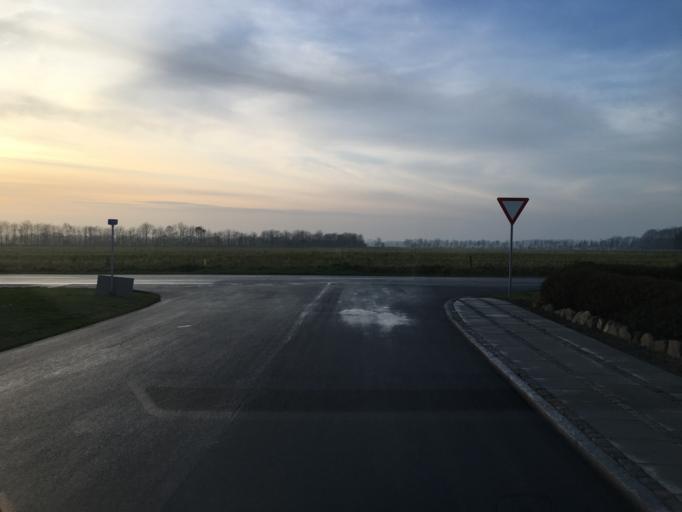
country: DK
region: South Denmark
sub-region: Tonder Kommune
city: Toftlund
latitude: 55.1262
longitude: 9.0629
